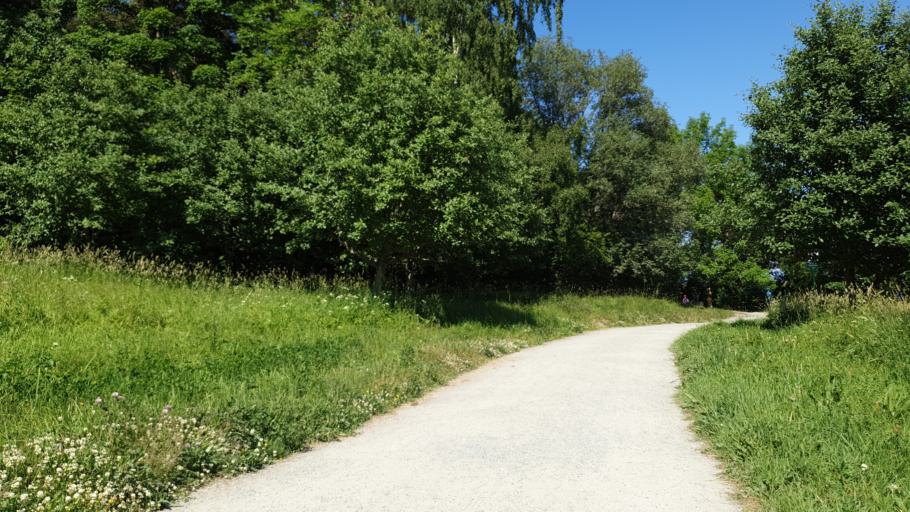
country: NO
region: Sor-Trondelag
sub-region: Trondheim
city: Trondheim
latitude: 63.4422
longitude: 10.4700
